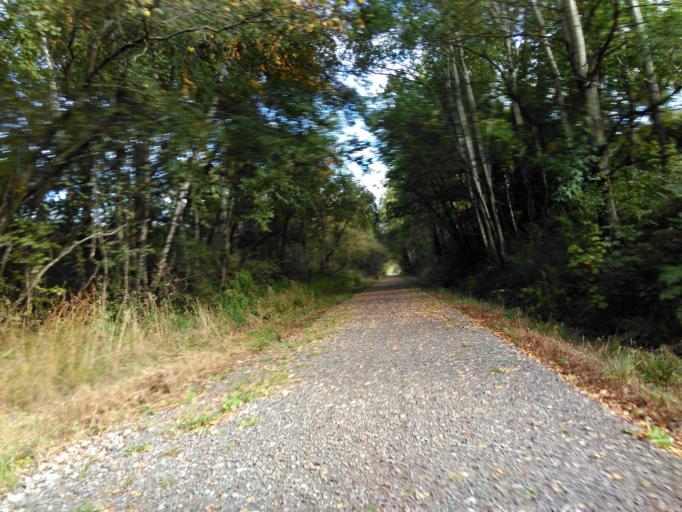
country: BE
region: Wallonia
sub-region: Province du Luxembourg
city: Vaux-sur-Sure
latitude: 49.9213
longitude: 5.5075
